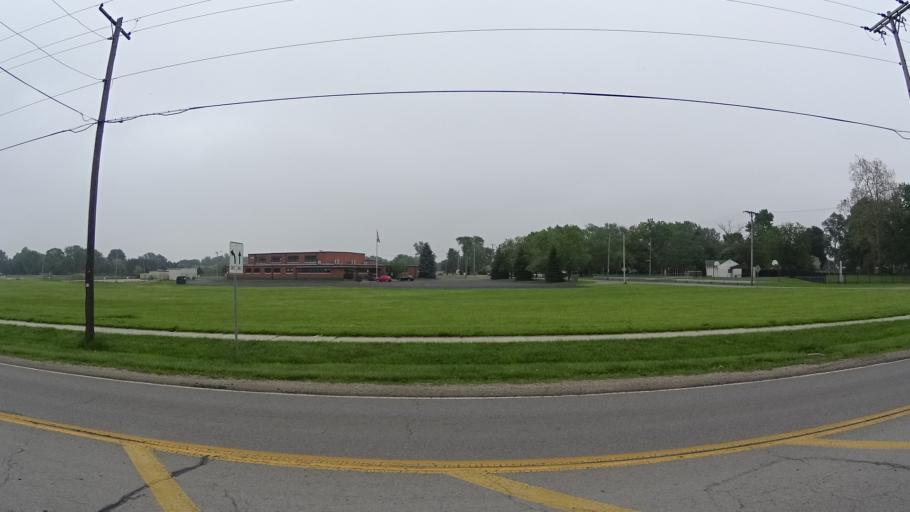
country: US
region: Ohio
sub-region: Erie County
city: Sandusky
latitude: 41.4206
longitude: -82.6908
